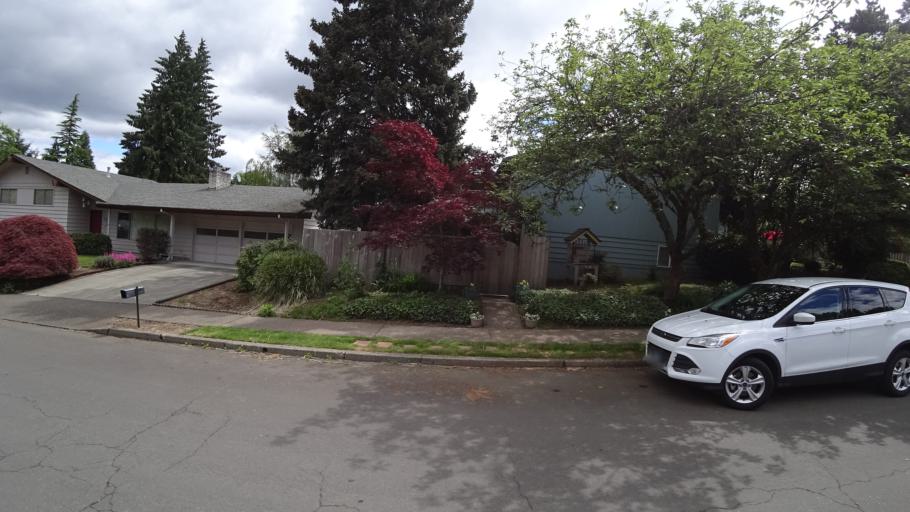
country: US
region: Oregon
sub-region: Washington County
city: Beaverton
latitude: 45.4646
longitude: -122.7996
